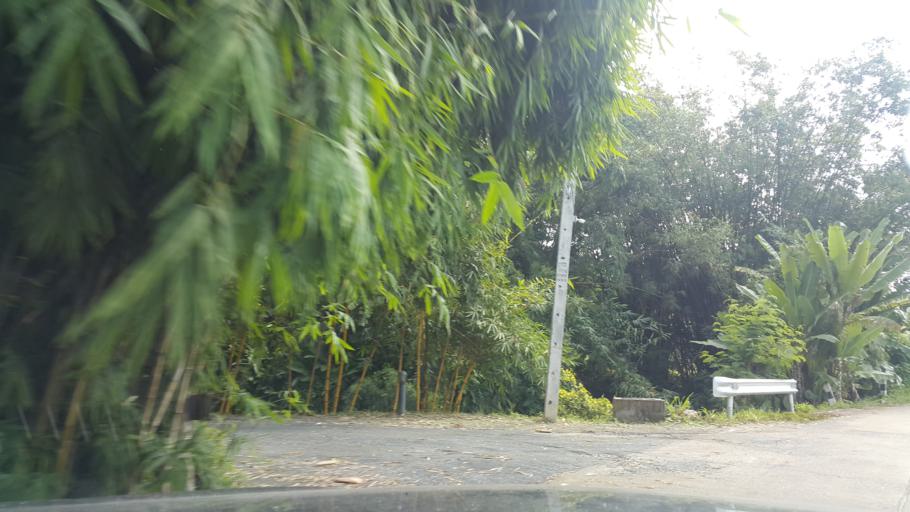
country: TH
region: Chiang Mai
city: San Sai
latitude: 18.9207
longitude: 99.1352
